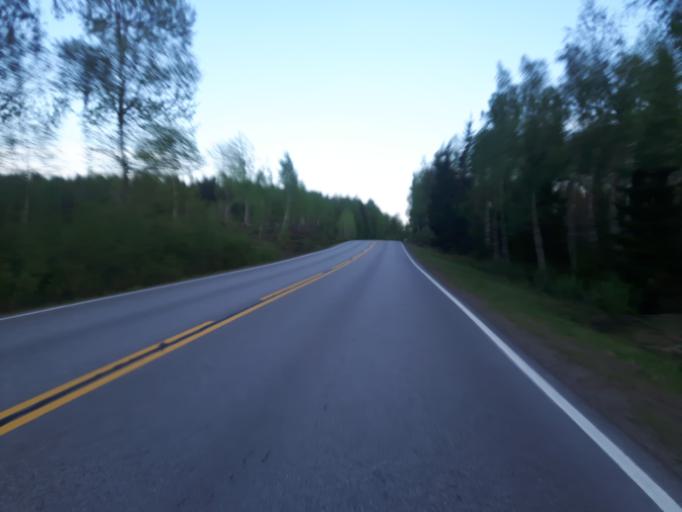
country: FI
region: Uusimaa
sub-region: Loviisa
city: Perna
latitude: 60.4583
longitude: 26.0753
